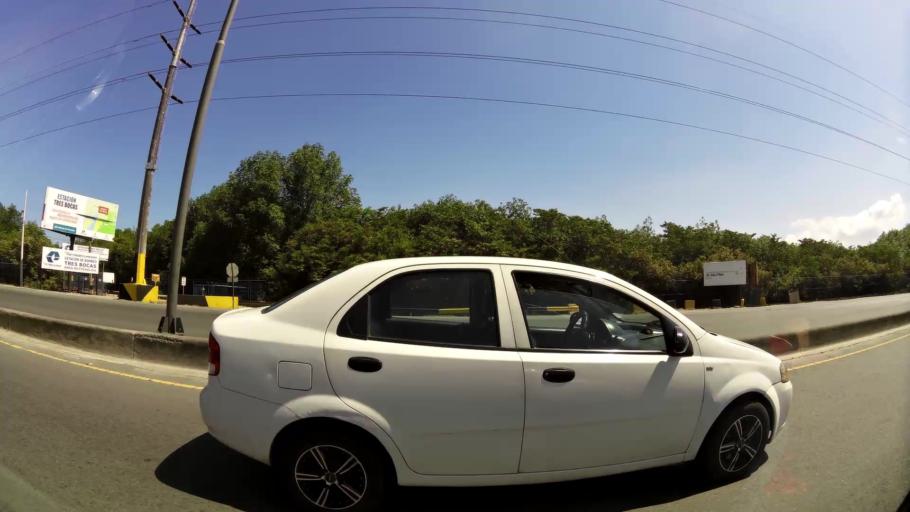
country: EC
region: Guayas
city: Guayaquil
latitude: -2.2252
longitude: -79.9564
